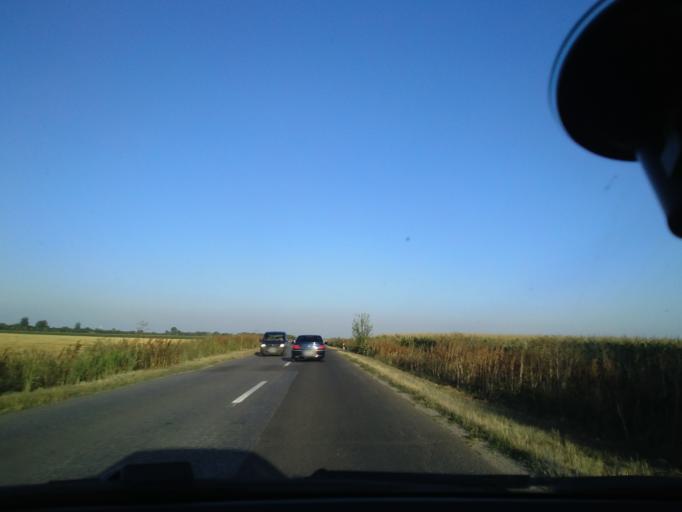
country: RS
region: Autonomna Pokrajina Vojvodina
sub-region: Juznobacki Okrug
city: Backi Petrovac
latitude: 45.3410
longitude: 19.6497
